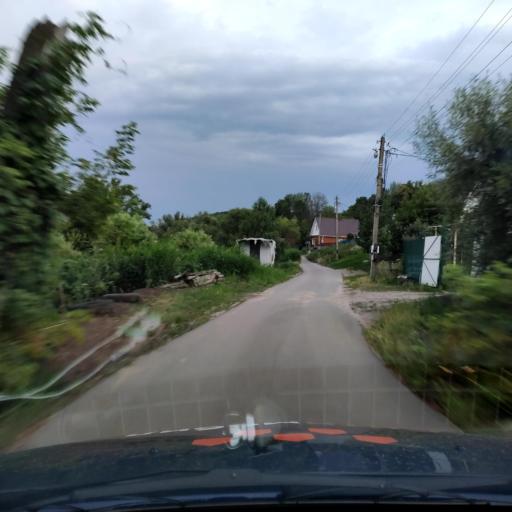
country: RU
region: Voronezj
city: Shilovo
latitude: 51.4526
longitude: 39.0309
